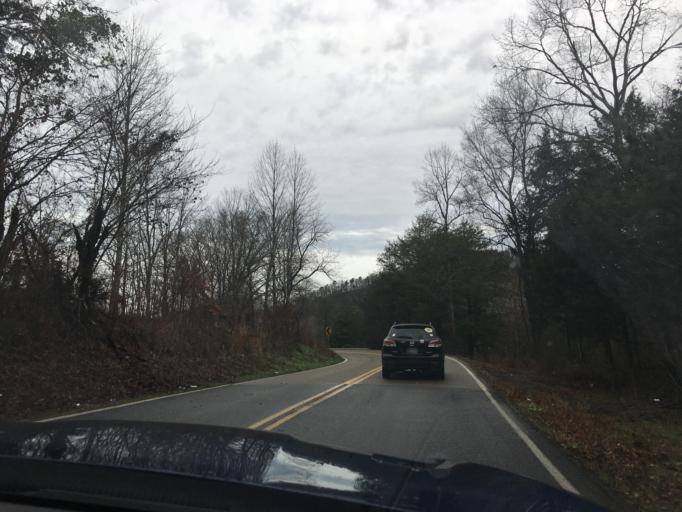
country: US
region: Tennessee
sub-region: McMinn County
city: Englewood
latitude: 35.3546
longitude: -84.4182
